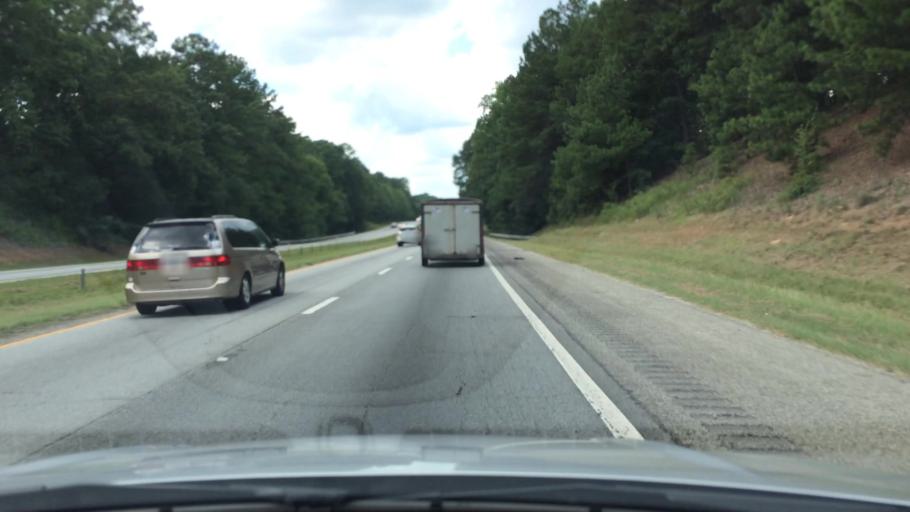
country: US
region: South Carolina
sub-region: Lexington County
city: Chapin
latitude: 34.2091
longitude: -81.3815
